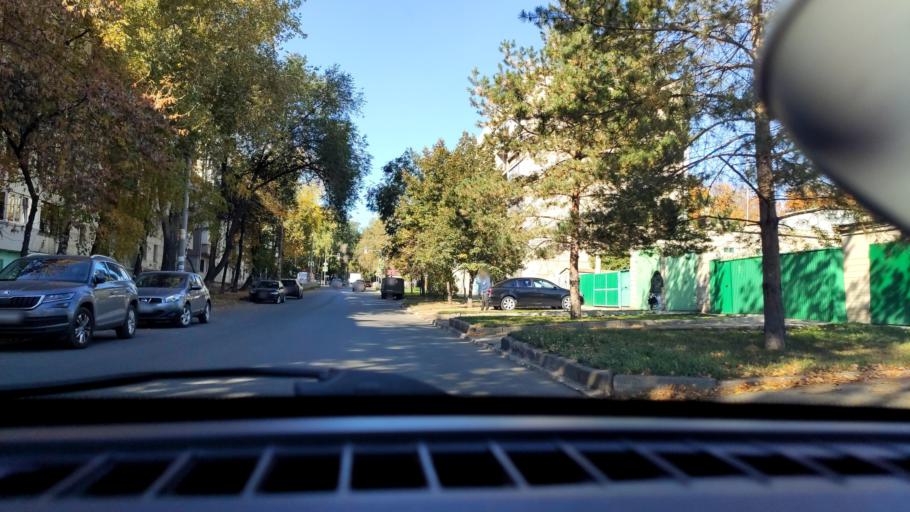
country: RU
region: Samara
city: Samara
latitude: 53.2104
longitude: 50.2371
